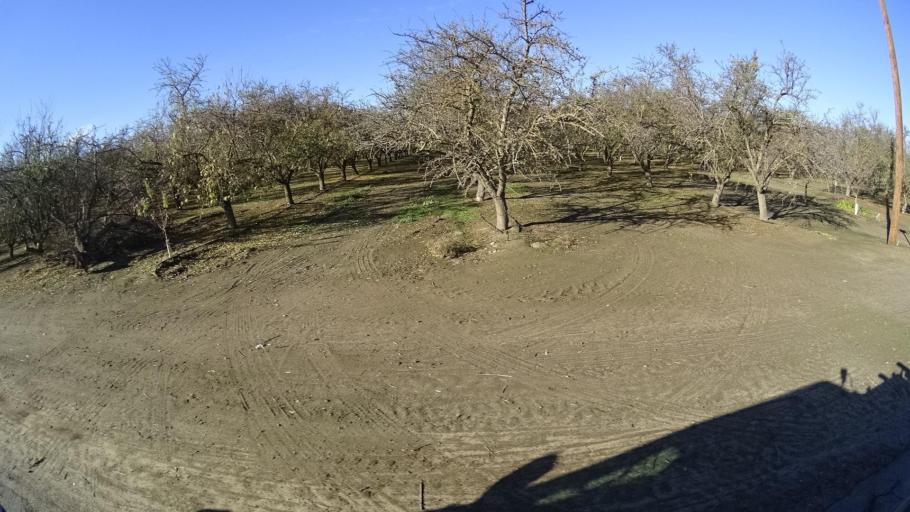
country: US
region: California
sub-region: Kern County
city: Delano
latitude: 35.7342
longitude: -119.2763
